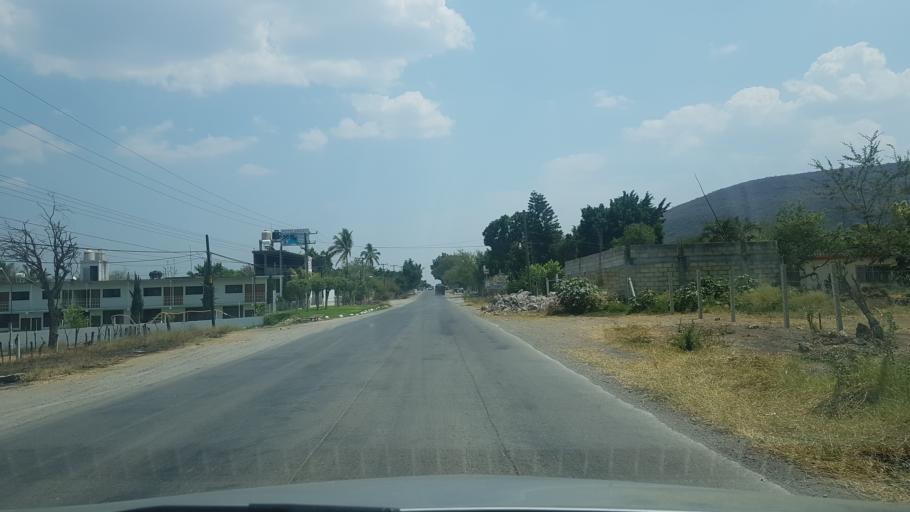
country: MX
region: Morelos
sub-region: Tlaltizapan de Zapata
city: Colonia Palo Prieto (Chipitongo)
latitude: 18.7247
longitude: -99.1226
